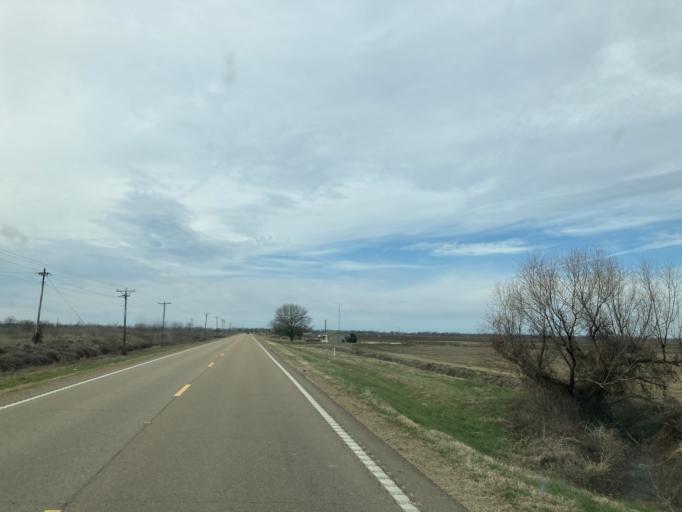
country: US
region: Mississippi
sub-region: Humphreys County
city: Belzoni
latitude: 33.1827
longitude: -90.6433
